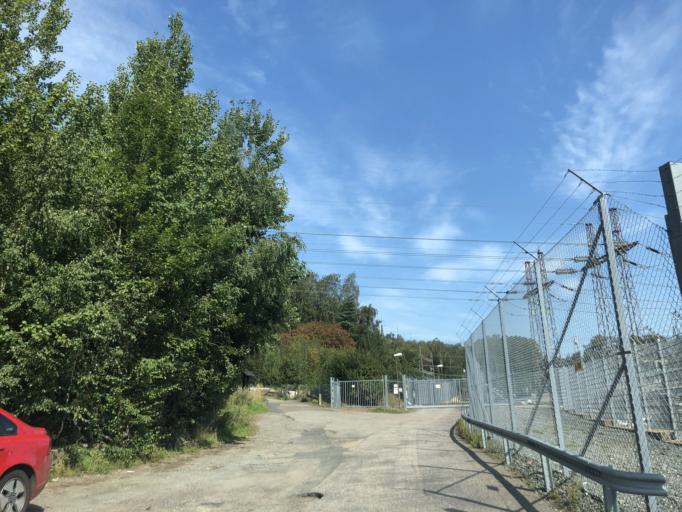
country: SE
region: Vaestra Goetaland
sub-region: Goteborg
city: Majorna
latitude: 57.7092
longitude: 11.8815
